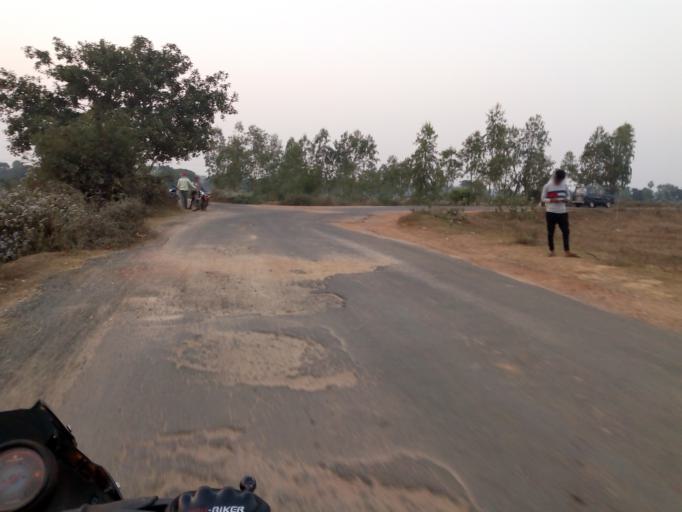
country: IN
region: West Bengal
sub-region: Bankura
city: Bankura
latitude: 23.2318
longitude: 87.0261
